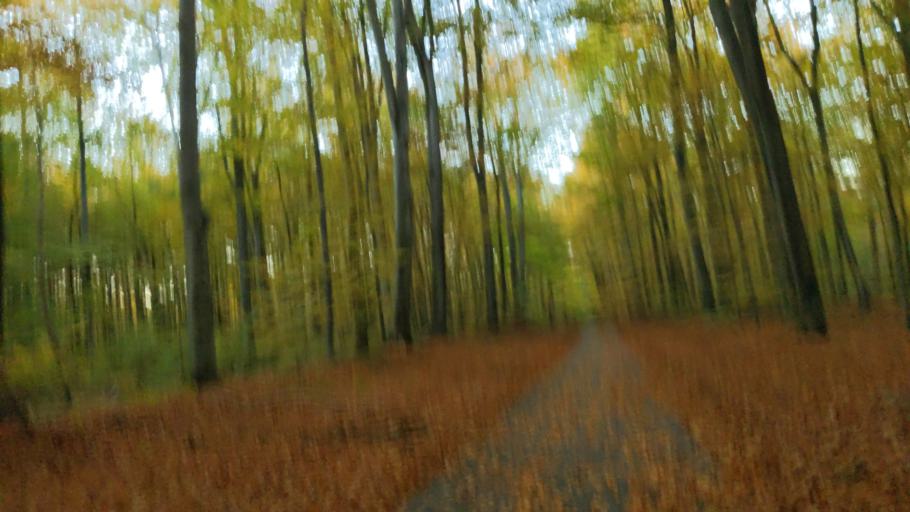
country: DE
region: Schleswig-Holstein
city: Bad Schwartau
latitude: 53.8829
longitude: 10.7510
